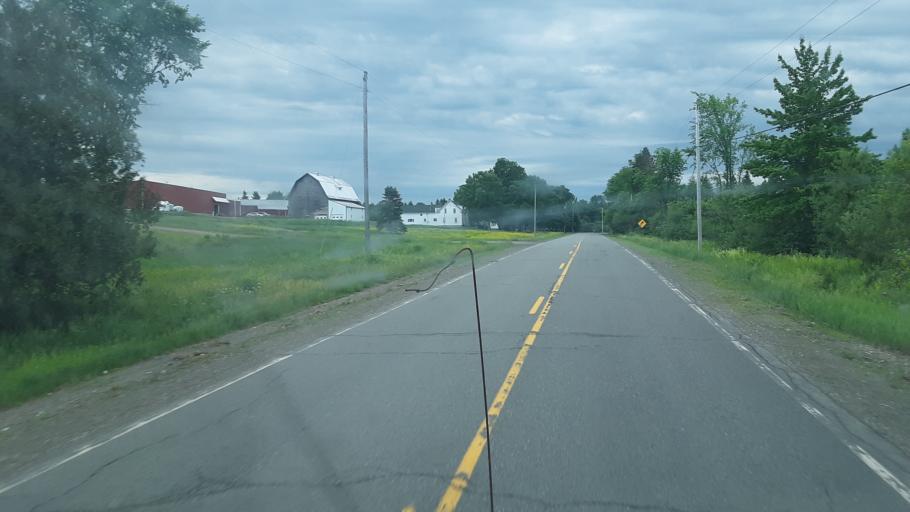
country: US
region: Maine
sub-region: Penobscot County
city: Patten
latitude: 45.8544
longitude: -68.3258
